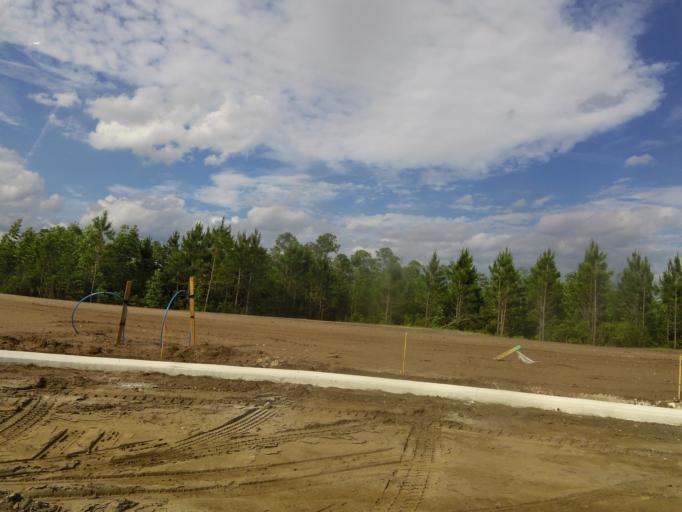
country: US
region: Florida
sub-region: Saint Johns County
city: Palm Valley
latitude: 30.1850
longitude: -81.5092
